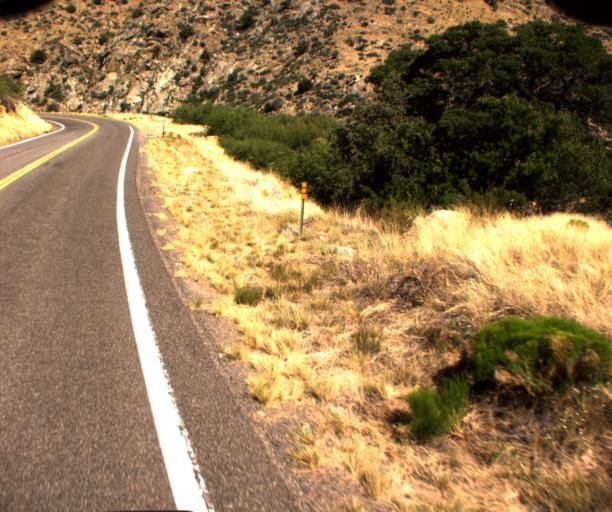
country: US
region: Arizona
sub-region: Graham County
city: Swift Trail Junction
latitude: 32.6790
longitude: -109.7748
